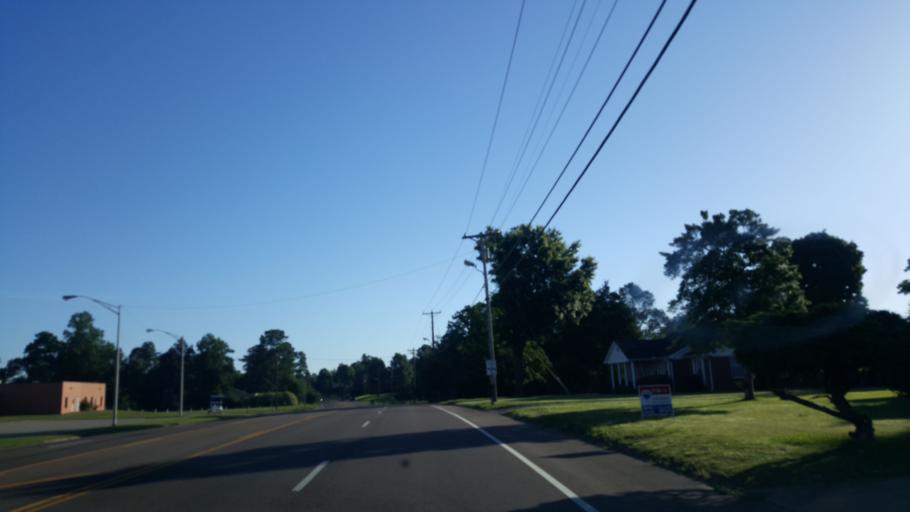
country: US
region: Tennessee
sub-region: Henderson County
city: Lexington
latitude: 35.6581
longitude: -88.3859
